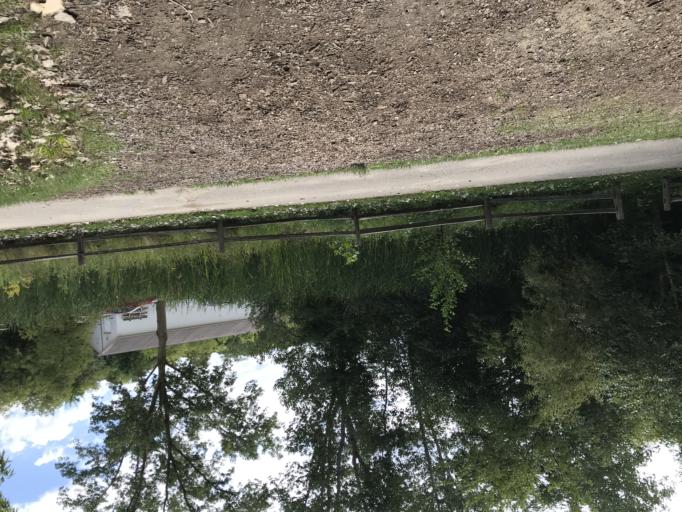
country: US
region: Michigan
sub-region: Washtenaw County
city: Ann Arbor
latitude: 42.2970
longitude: -83.7438
